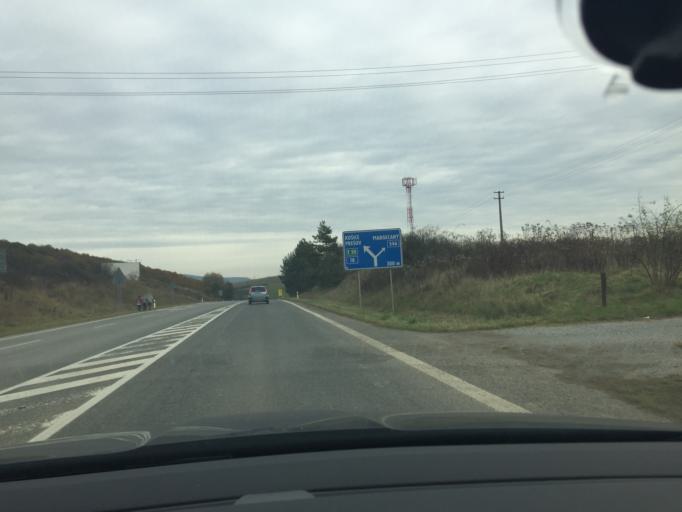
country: SK
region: Presovsky
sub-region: Okres Presov
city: Presov
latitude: 49.0016
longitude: 21.1919
